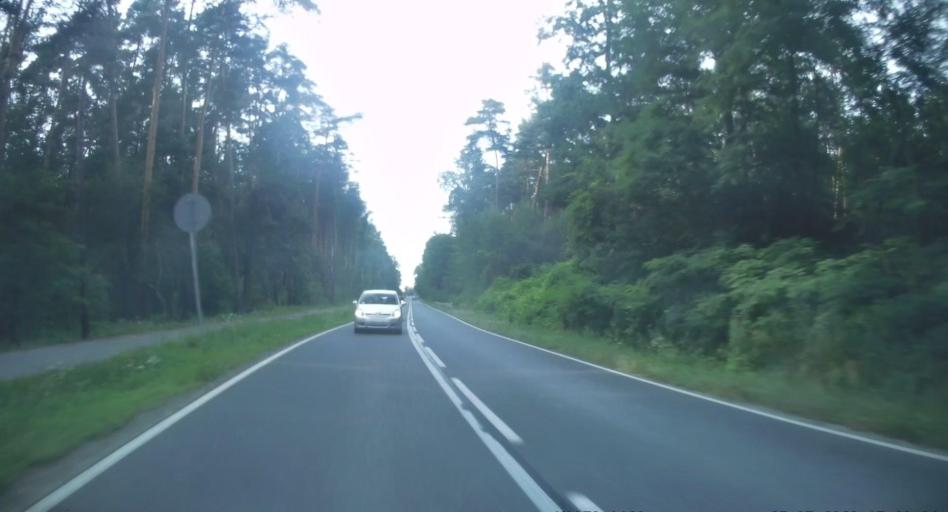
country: PL
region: Lesser Poland Voivodeship
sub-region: Powiat brzeski
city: Przyborow
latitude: 50.0520
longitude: 20.6389
